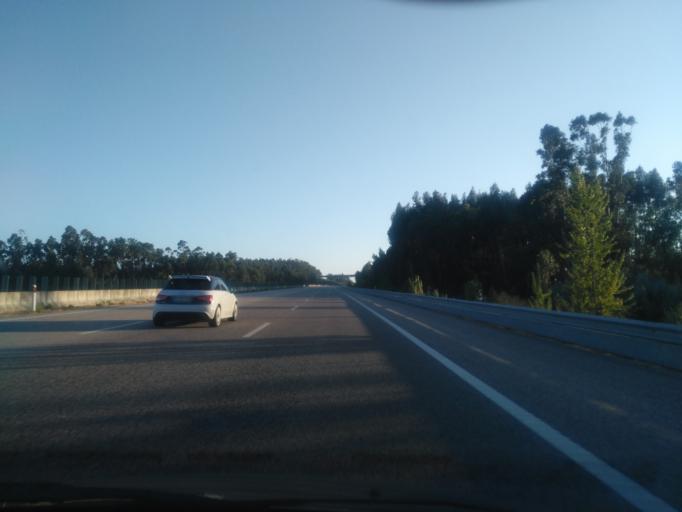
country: PT
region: Coimbra
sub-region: Figueira da Foz
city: Lavos
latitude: 40.0864
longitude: -8.7658
